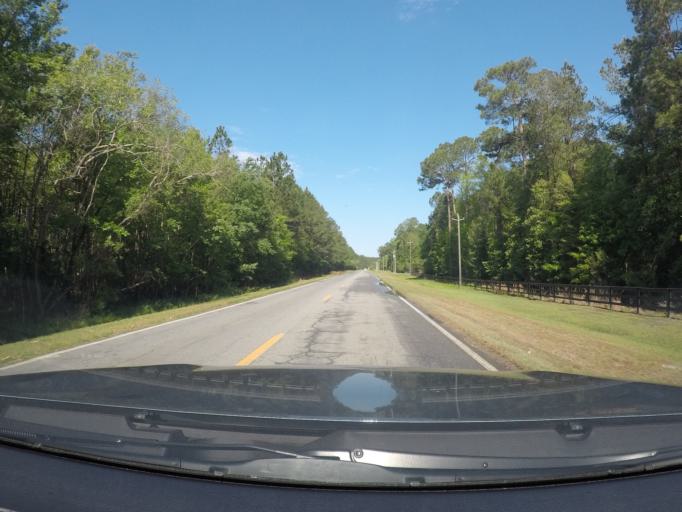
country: US
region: Georgia
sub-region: Chatham County
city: Bloomingdale
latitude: 32.0576
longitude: -81.3047
